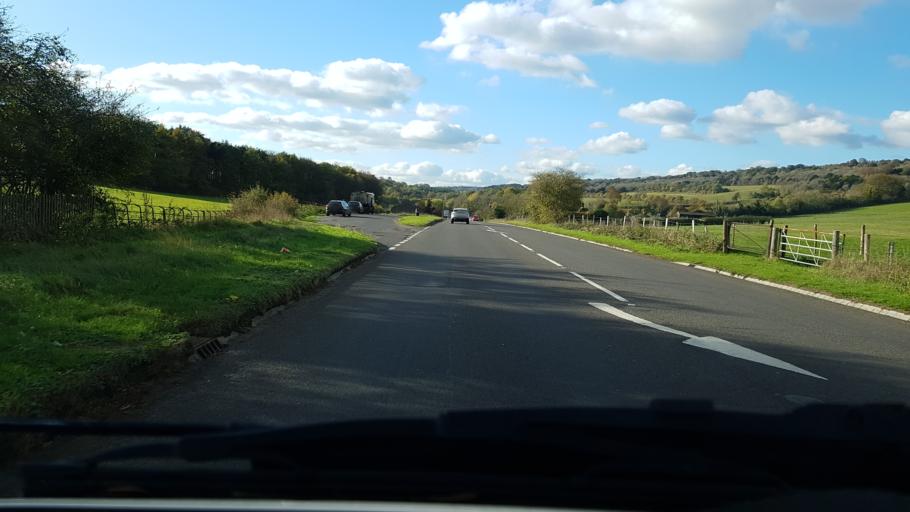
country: GB
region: England
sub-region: Surrey
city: Chilworth
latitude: 51.2235
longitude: -0.4747
